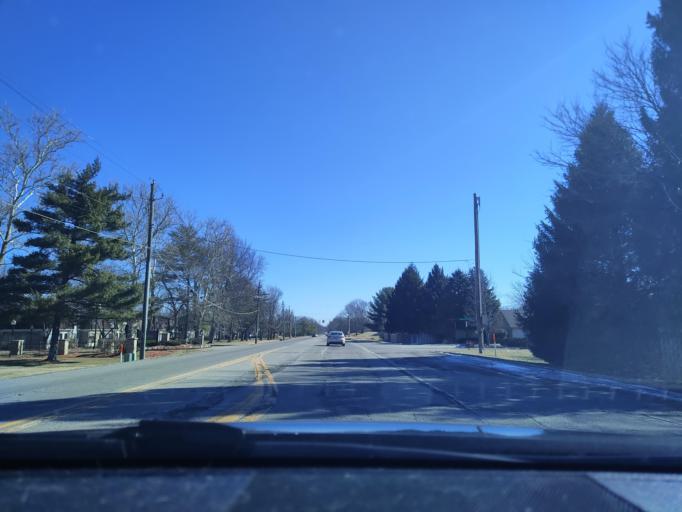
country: US
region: Indiana
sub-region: Marion County
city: Meridian Hills
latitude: 39.8974
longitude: -86.1959
